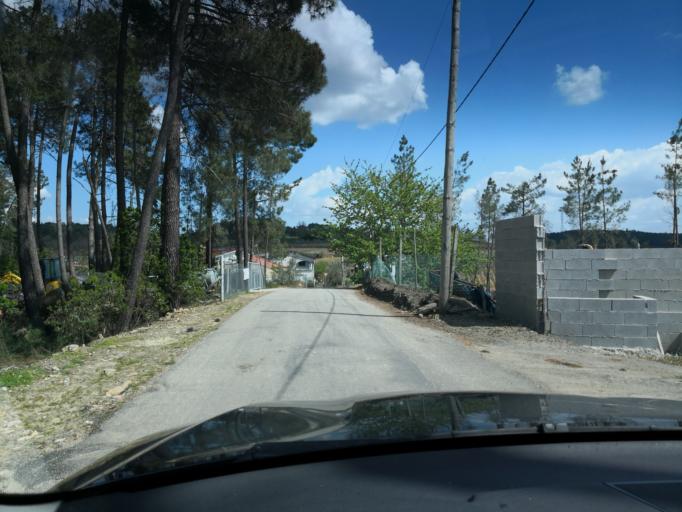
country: PT
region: Vila Real
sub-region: Sabrosa
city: Vilela
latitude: 41.2247
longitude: -7.6833
